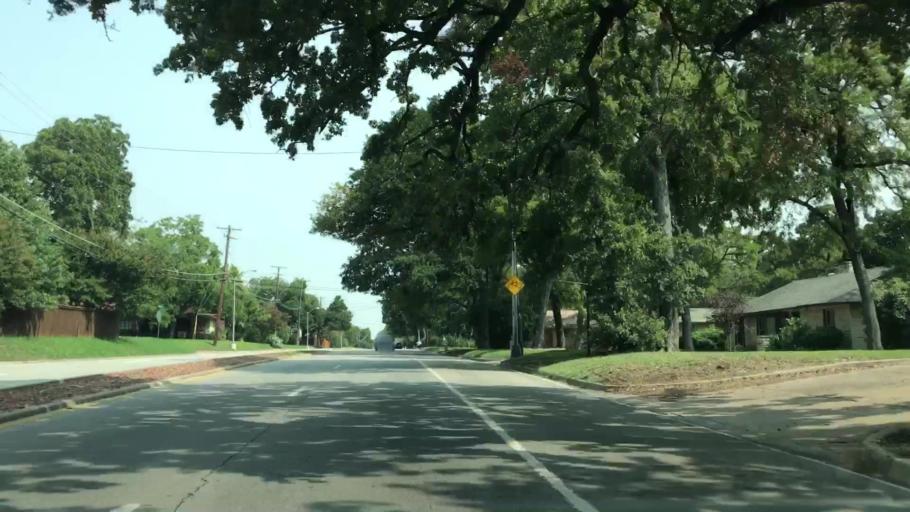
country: US
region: Texas
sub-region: Dallas County
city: Dallas
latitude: 32.7604
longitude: -96.8356
